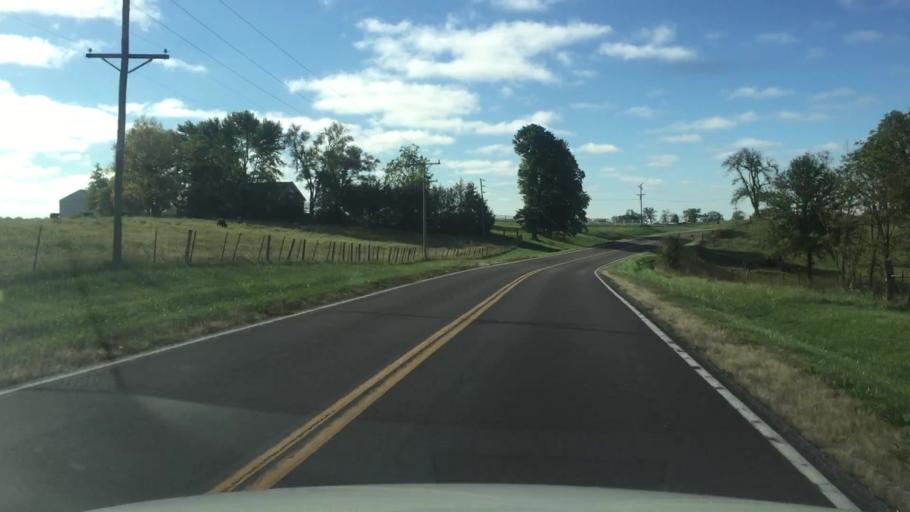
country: US
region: Missouri
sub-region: Howard County
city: New Franklin
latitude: 39.0907
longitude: -92.7434
